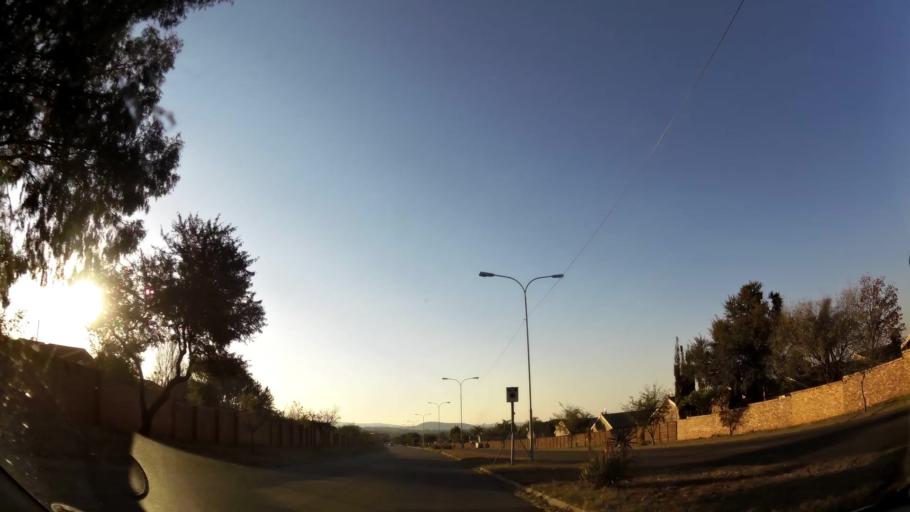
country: ZA
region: Gauteng
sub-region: City of Tshwane Metropolitan Municipality
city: Centurion
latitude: -25.8778
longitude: 28.1406
